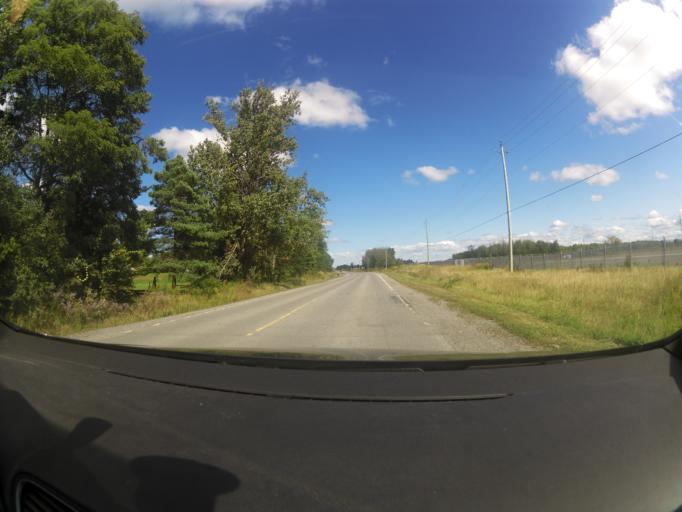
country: CA
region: Ontario
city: Carleton Place
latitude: 45.1628
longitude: -76.0711
